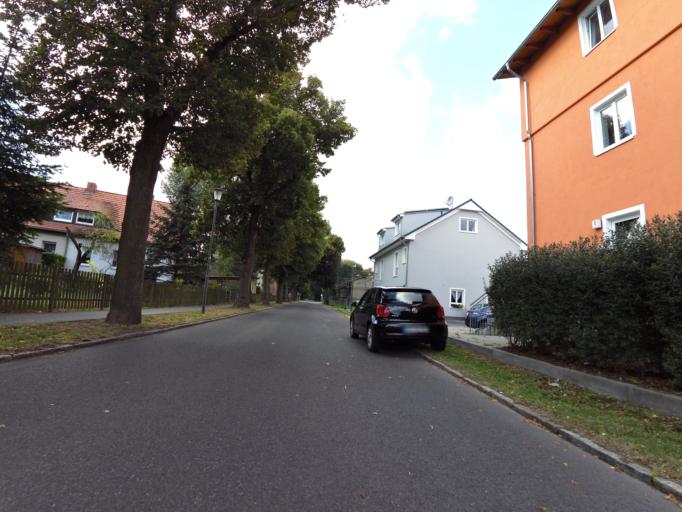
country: DE
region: Brandenburg
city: Grossbeeren
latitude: 52.3609
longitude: 13.3266
